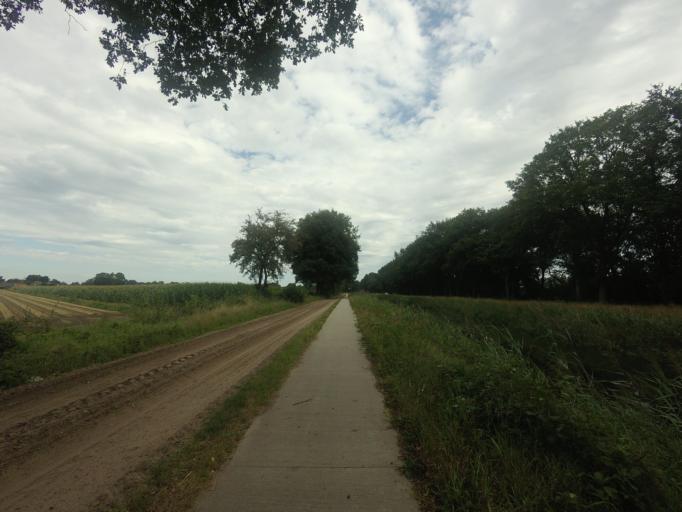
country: NL
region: Overijssel
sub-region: Gemeente Raalte
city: Raalte
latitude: 52.4315
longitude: 6.3258
